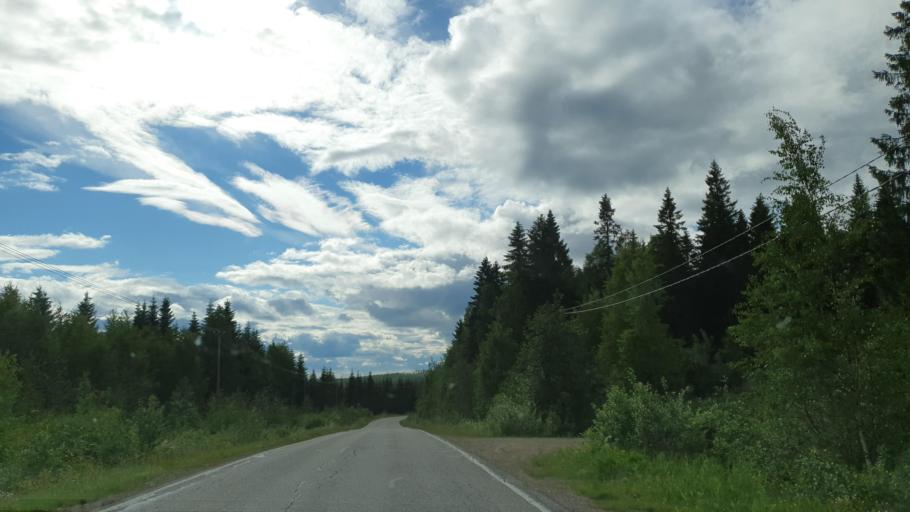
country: FI
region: Kainuu
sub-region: Kajaani
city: Ristijaervi
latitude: 64.3374
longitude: 28.0662
